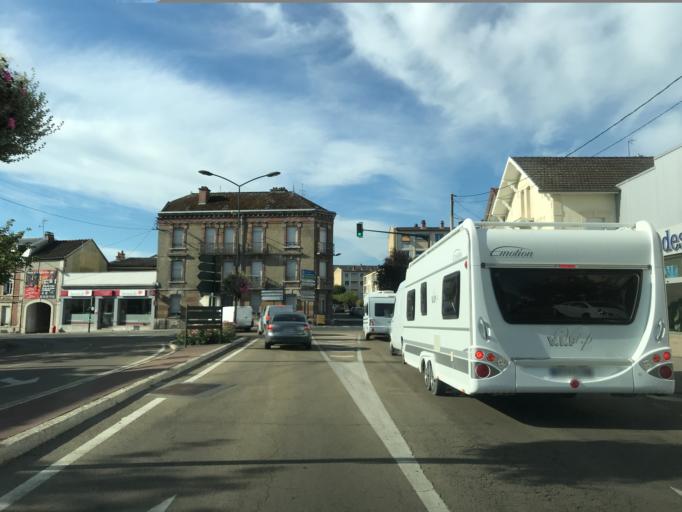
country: FR
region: Champagne-Ardenne
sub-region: Departement de la Marne
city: Epernay
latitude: 49.0488
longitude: 3.9530
